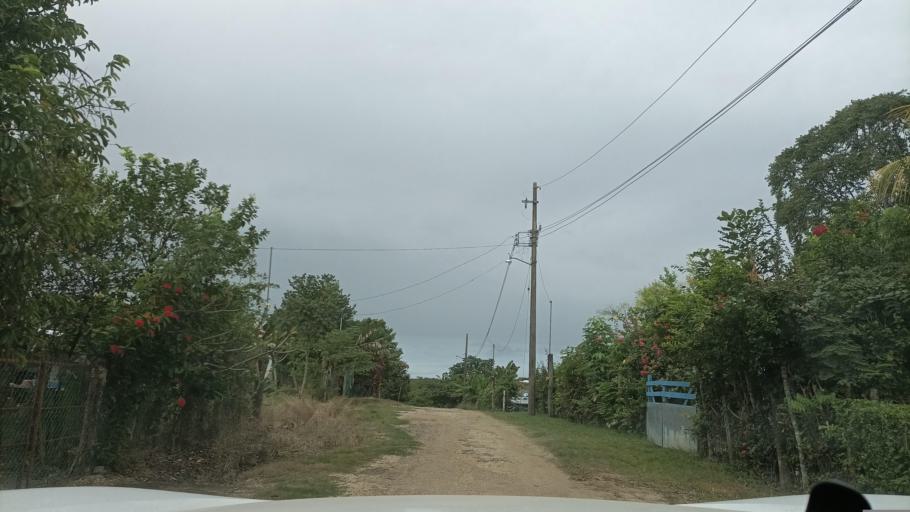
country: MX
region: Veracruz
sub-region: Jaltipan
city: Las Lomas de Tacamichapan
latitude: 17.8635
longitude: -94.7118
